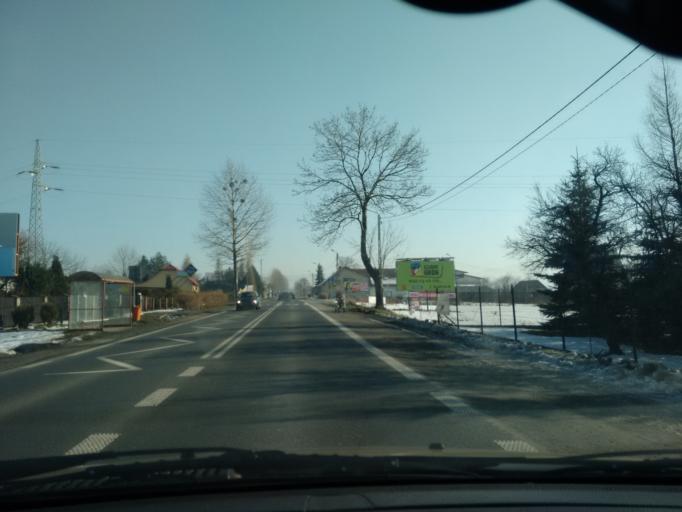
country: PL
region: Lesser Poland Voivodeship
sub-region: Powiat wadowicki
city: Roczyny
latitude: 49.8649
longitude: 19.3131
